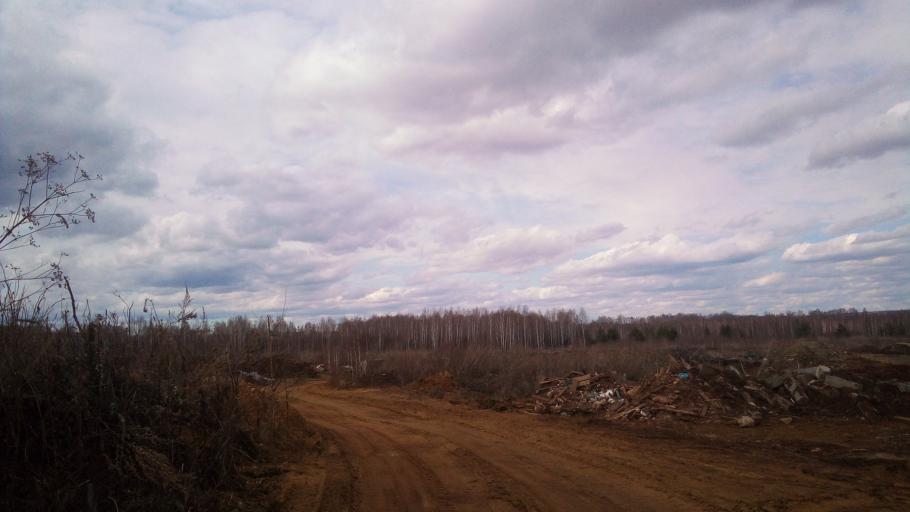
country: RU
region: Chelyabinsk
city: Sargazy
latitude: 55.1253
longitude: 61.2582
